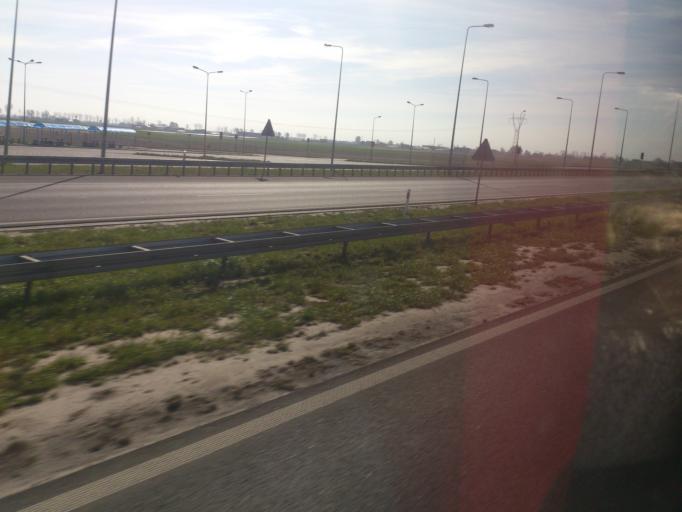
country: PL
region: Kujawsko-Pomorskie
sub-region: Powiat aleksandrowski
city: Waganiec
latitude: 52.7609
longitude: 18.8550
